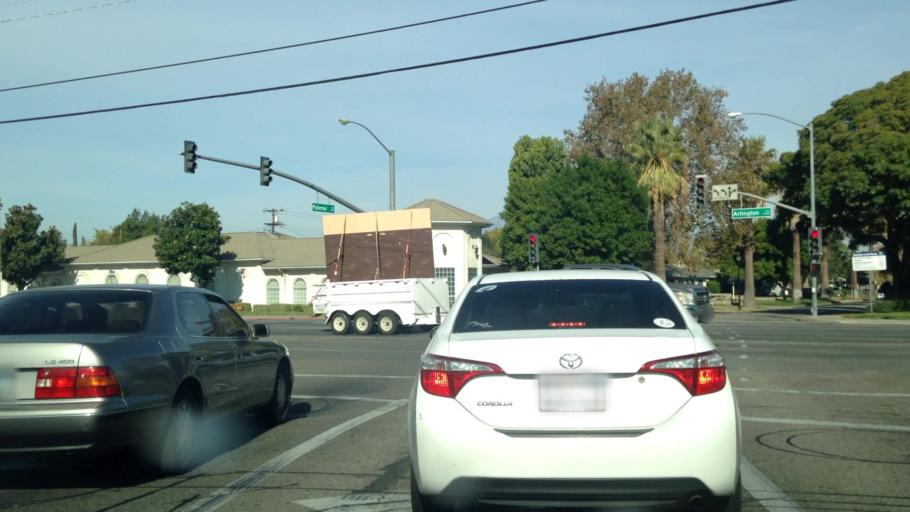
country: US
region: California
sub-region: Riverside County
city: Riverside
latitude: 33.9459
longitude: -117.4130
